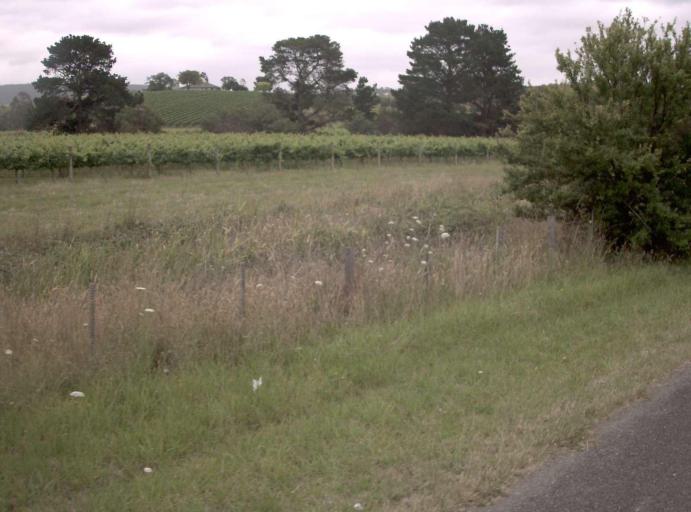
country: AU
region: Victoria
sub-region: Yarra Ranges
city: Yarra Glen
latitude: -37.6386
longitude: 145.3999
